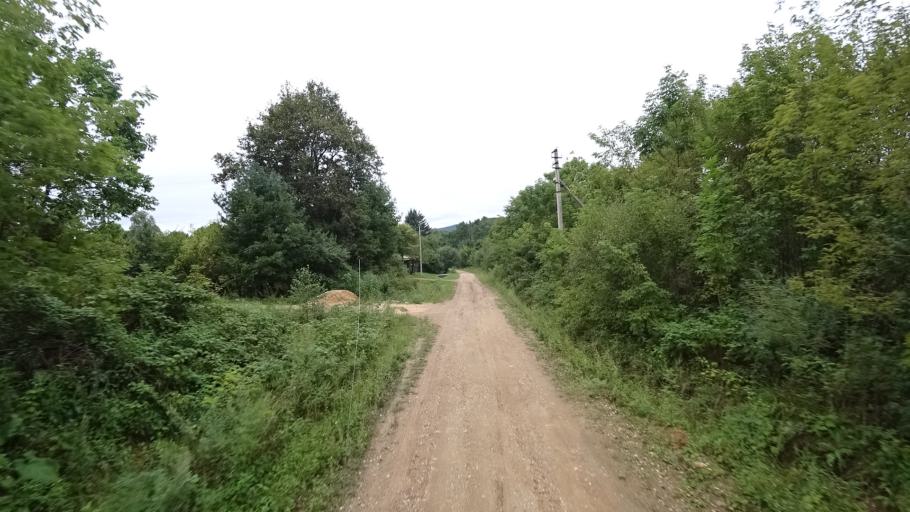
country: RU
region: Primorskiy
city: Rettikhovka
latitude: 44.1608
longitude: 132.7432
